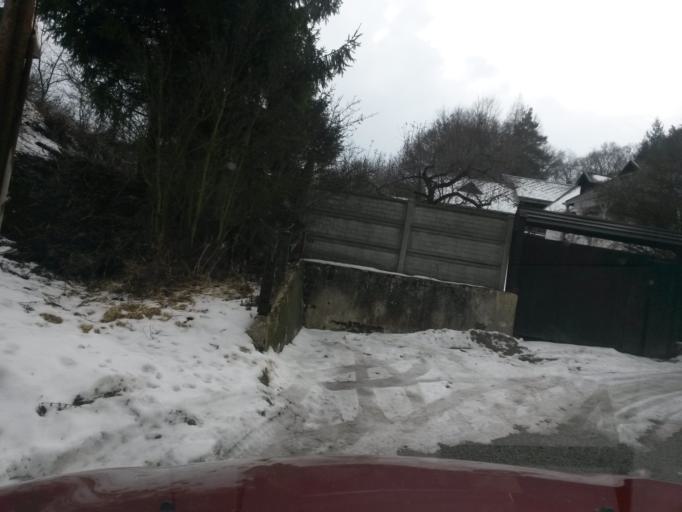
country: SK
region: Presovsky
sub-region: Okres Presov
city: Presov
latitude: 48.8612
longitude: 21.2306
